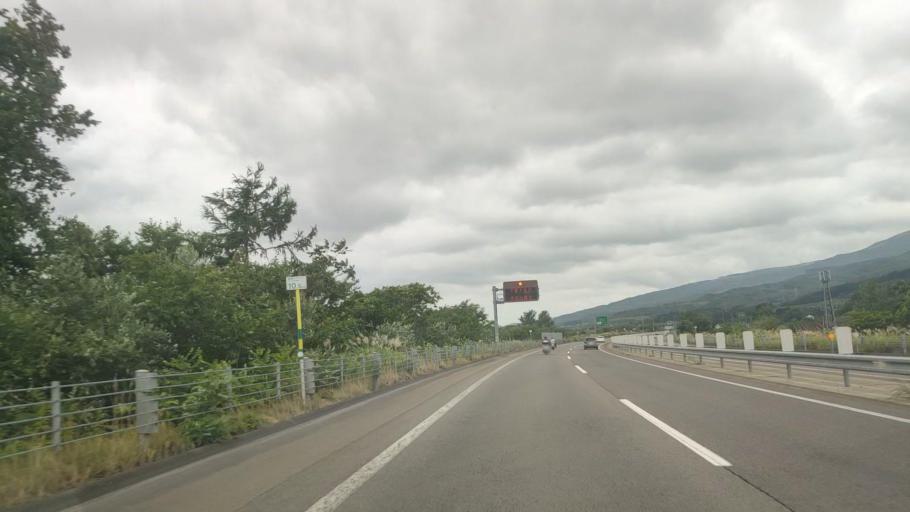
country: JP
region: Hokkaido
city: Nanae
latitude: 41.8625
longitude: 140.7318
